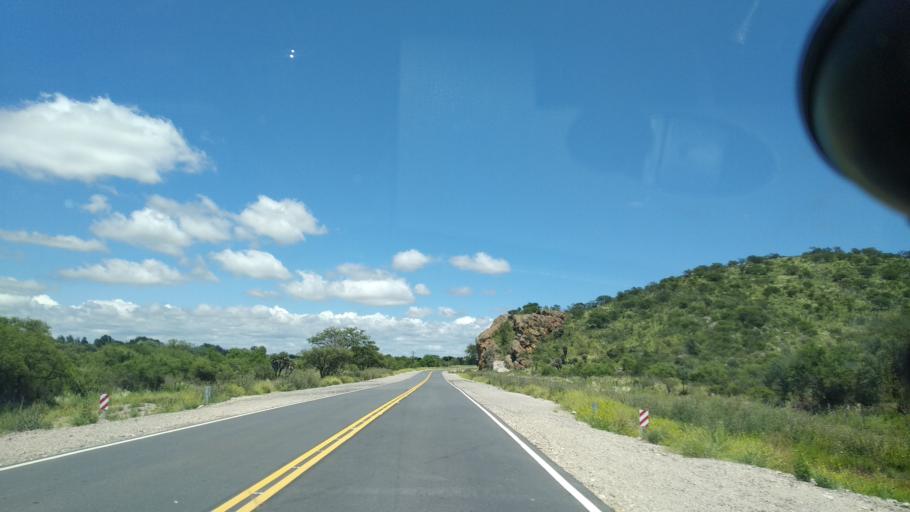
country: AR
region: Cordoba
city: Salsacate
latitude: -31.3463
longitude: -65.1017
